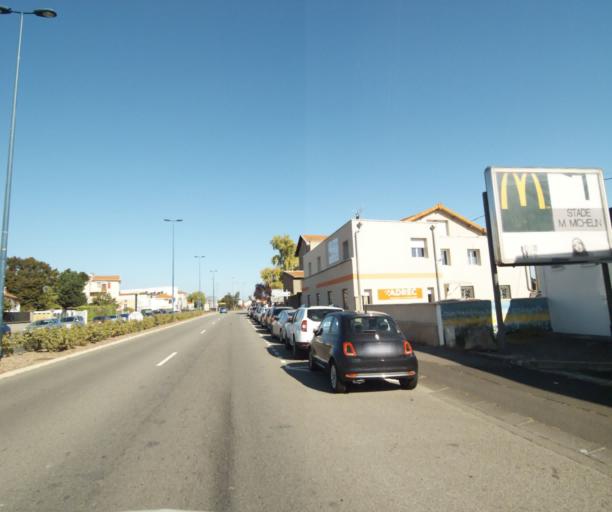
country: FR
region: Auvergne
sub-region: Departement du Puy-de-Dome
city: Clermont-Ferrand
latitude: 45.7903
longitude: 3.1180
